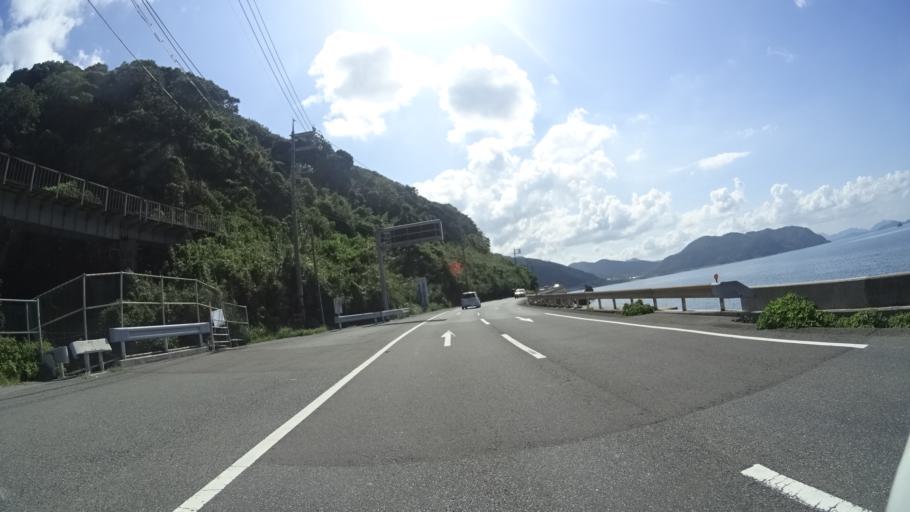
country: JP
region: Yamaguchi
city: Shimonoseki
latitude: 34.2444
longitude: 130.9156
